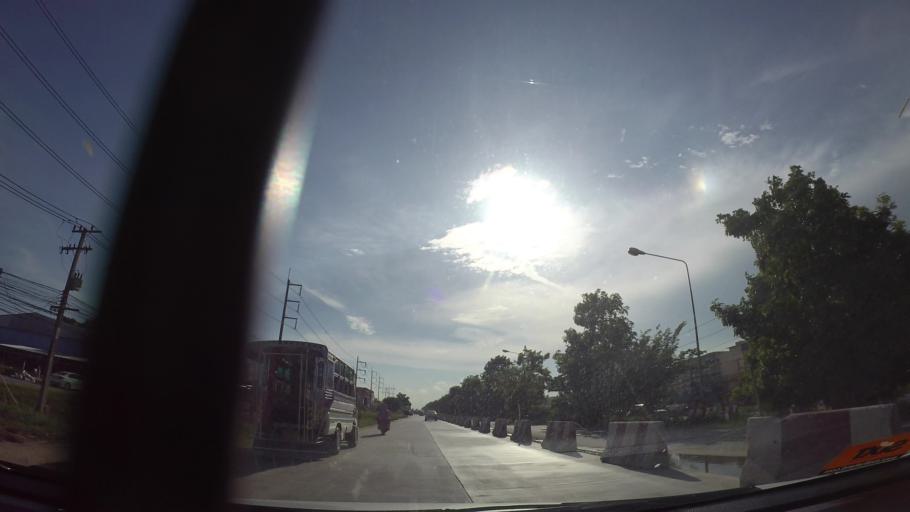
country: TH
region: Rayong
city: Rayong
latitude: 12.6963
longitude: 101.2814
